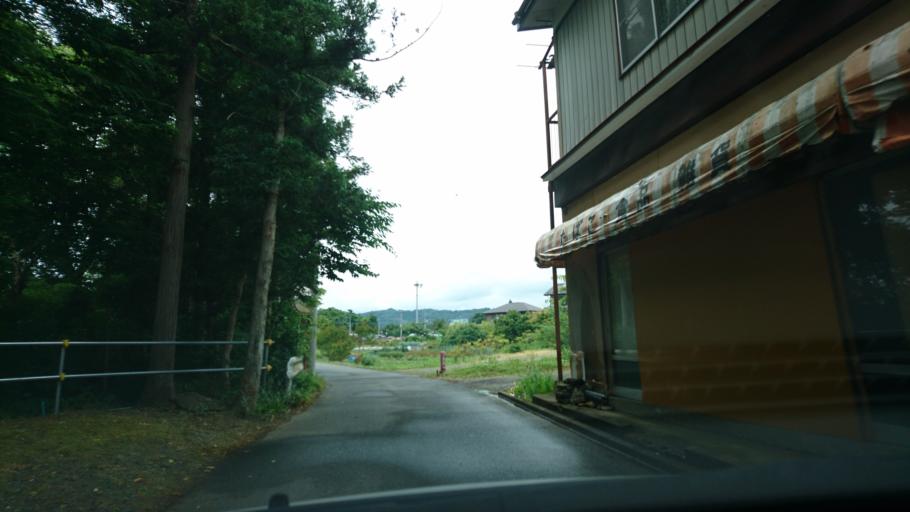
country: JP
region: Iwate
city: Ichinoseki
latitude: 38.9301
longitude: 141.1106
